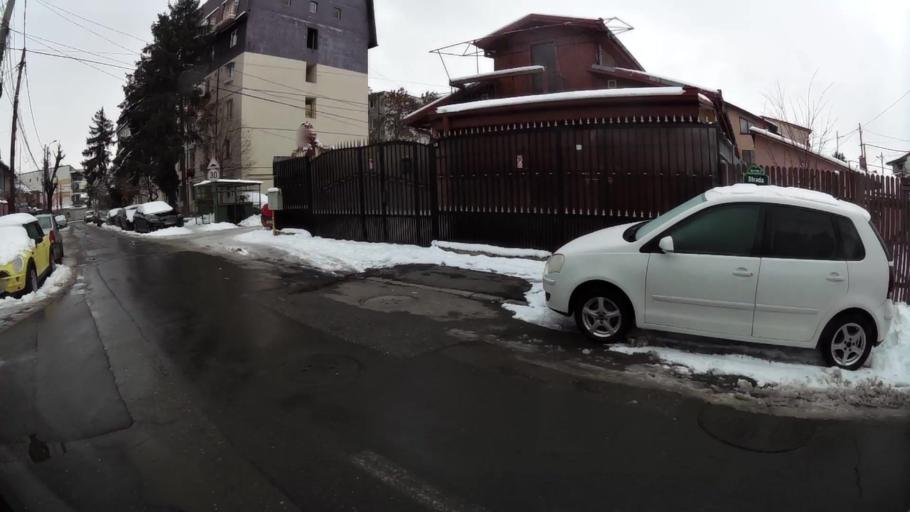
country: RO
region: Bucuresti
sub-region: Municipiul Bucuresti
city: Bucuresti
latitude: 44.3921
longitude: 26.1052
